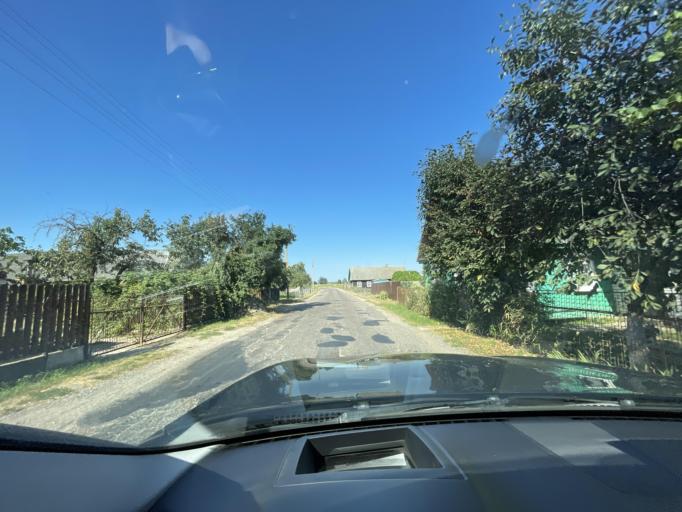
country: BY
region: Grodnenskaya
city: Hrodna
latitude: 53.7188
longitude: 23.9865
